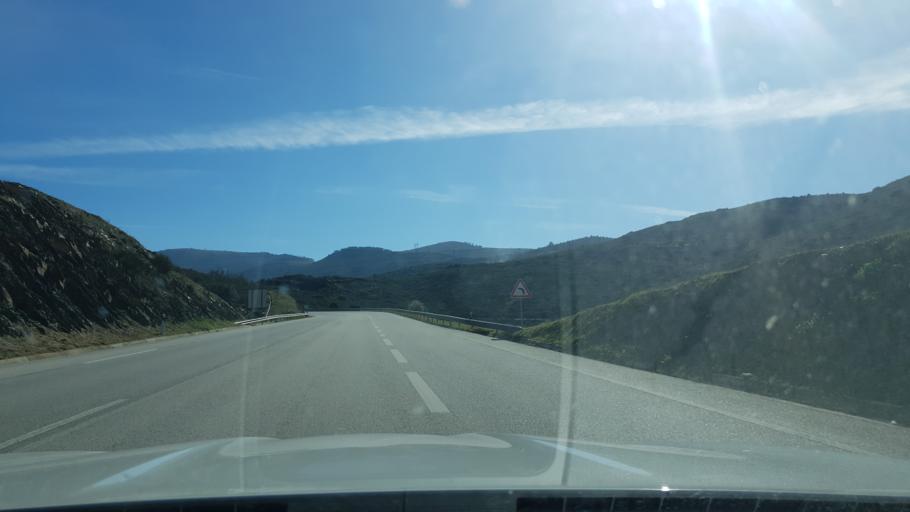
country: PT
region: Braganca
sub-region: Torre de Moncorvo
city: Torre de Moncorvo
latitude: 41.1832
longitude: -7.0901
